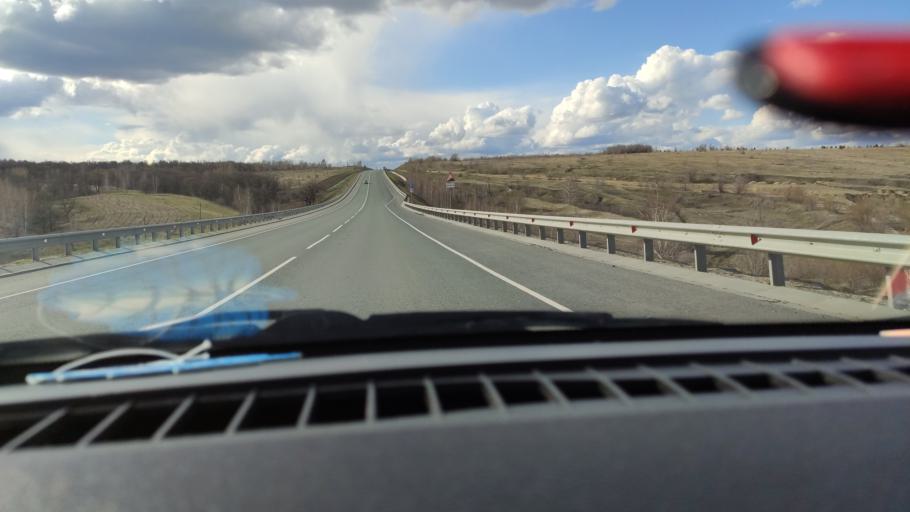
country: RU
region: Saratov
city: Shikhany
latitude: 52.1409
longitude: 47.2073
